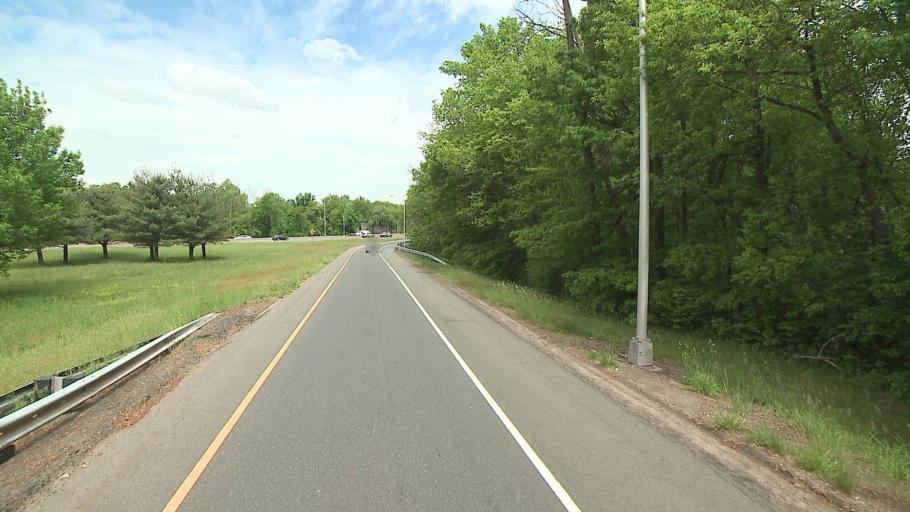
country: US
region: Connecticut
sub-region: Hartford County
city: Thompsonville
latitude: 41.9924
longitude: -72.5860
